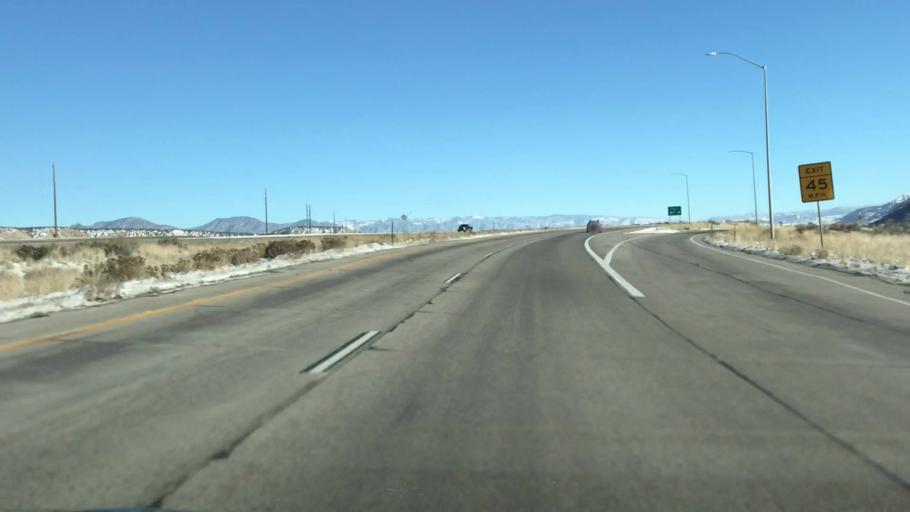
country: US
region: Colorado
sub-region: Garfield County
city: Rifle
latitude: 39.5217
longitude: -107.8503
